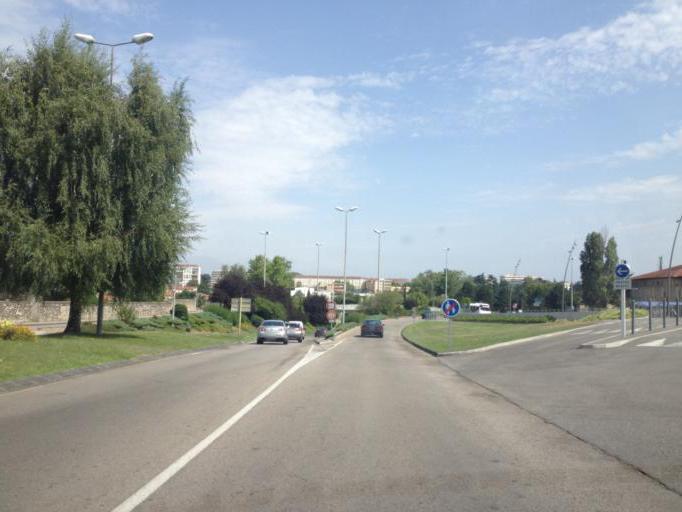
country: FR
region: Rhone-Alpes
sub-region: Departement de la Drome
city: Romans-sur-Isere
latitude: 45.0387
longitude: 5.0557
